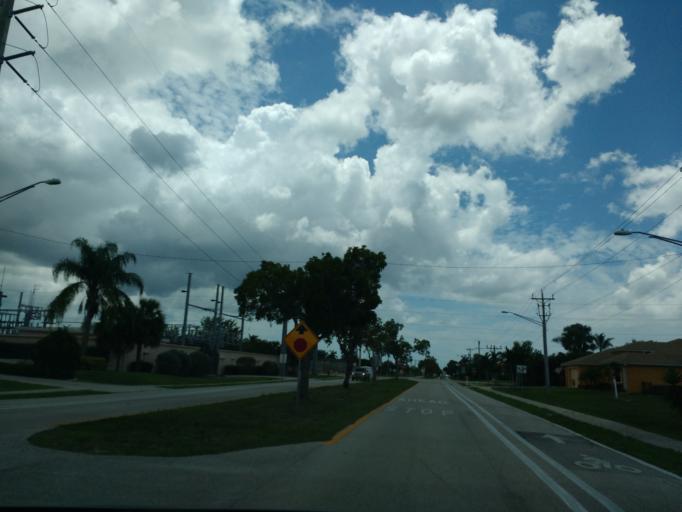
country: US
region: Florida
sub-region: Lee County
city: Cape Coral
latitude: 26.5640
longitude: -82.0173
